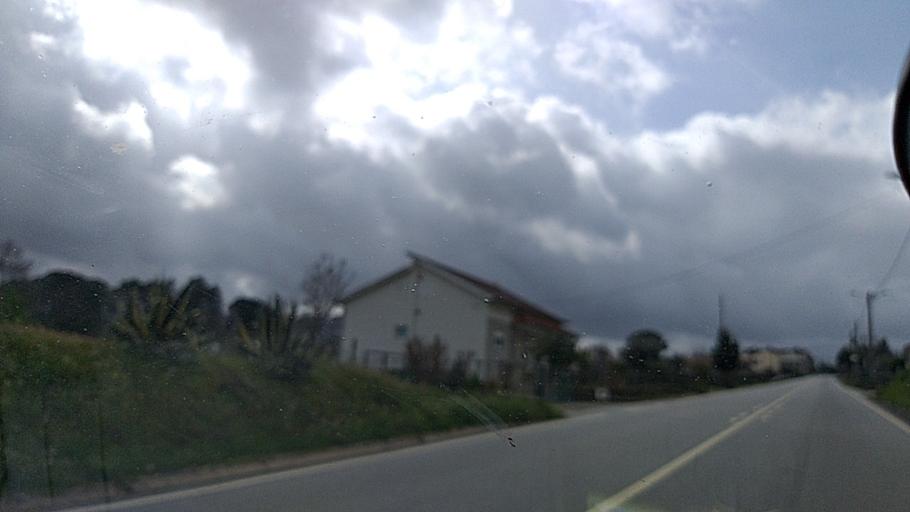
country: PT
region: Viseu
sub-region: Mangualde
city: Mangualde
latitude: 40.6314
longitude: -7.7477
